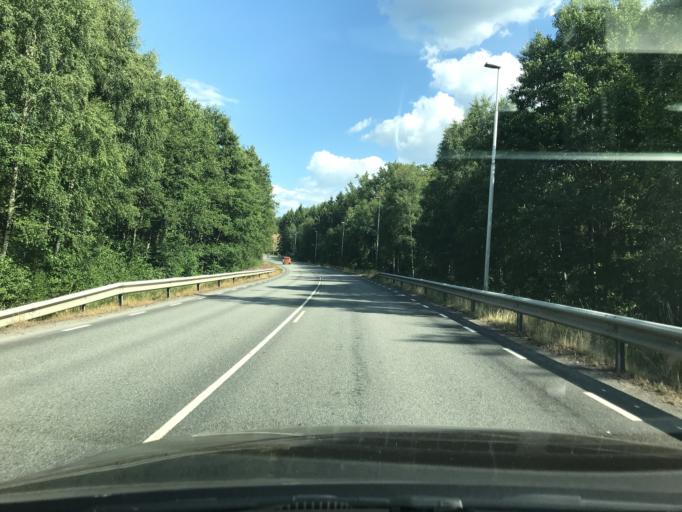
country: SE
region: Skane
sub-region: Hassleholms Kommun
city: Hastveda
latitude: 56.2780
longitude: 13.9351
